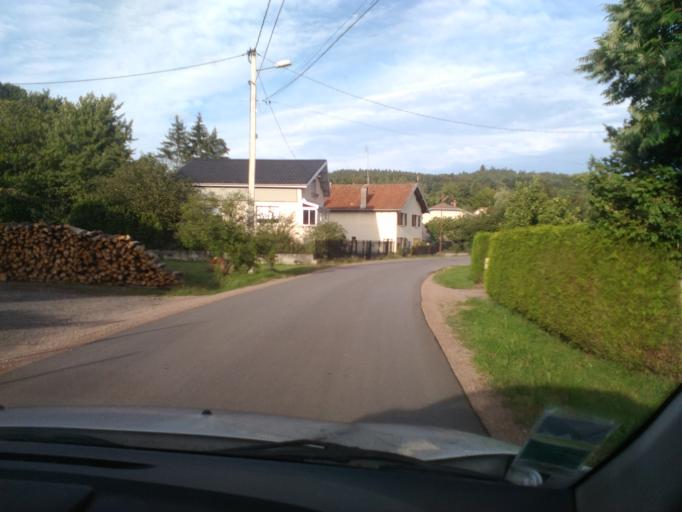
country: FR
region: Lorraine
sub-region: Departement des Vosges
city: Jeanmenil
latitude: 48.3128
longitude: 6.7084
